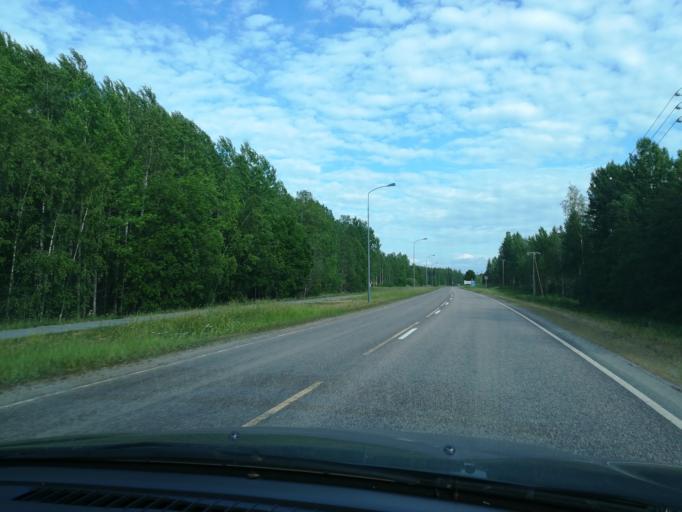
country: FI
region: South Karelia
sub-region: Imatra
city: Imatra
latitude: 61.1573
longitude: 28.7952
